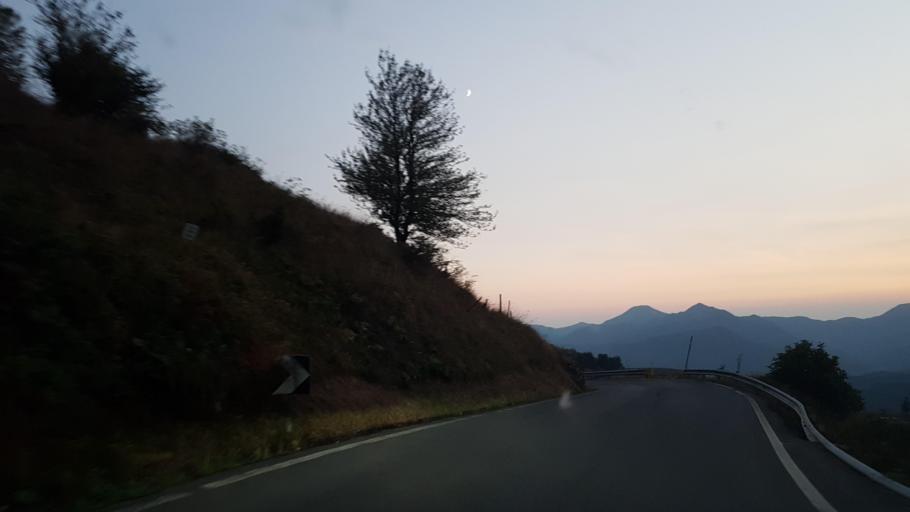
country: IT
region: Liguria
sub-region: Provincia di La Spezia
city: Varese Ligure
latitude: 44.4122
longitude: 9.6301
